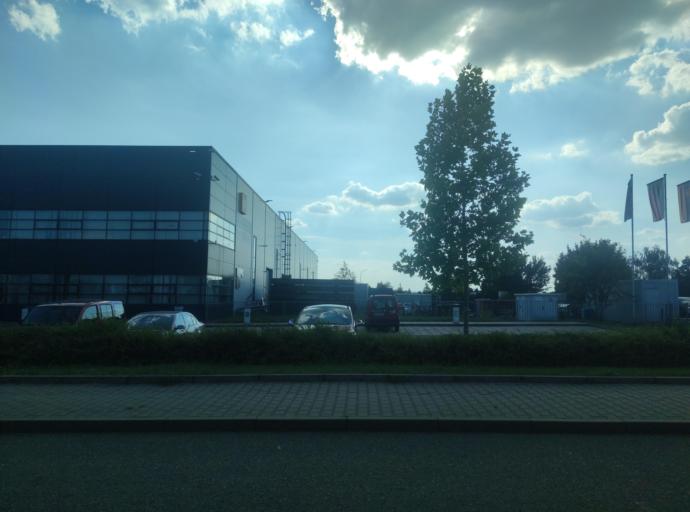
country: CZ
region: South Moravian
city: Podoli
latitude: 49.1712
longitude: 16.6737
